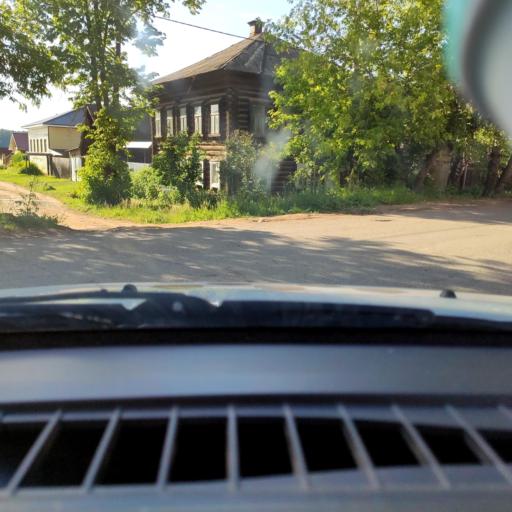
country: RU
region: Perm
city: Ocher
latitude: 57.8849
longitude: 54.7117
